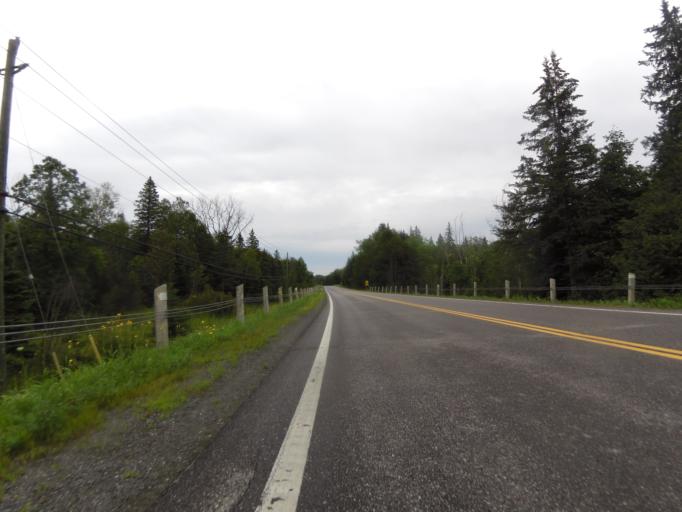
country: CA
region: Ontario
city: Perth
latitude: 45.0301
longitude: -76.3871
